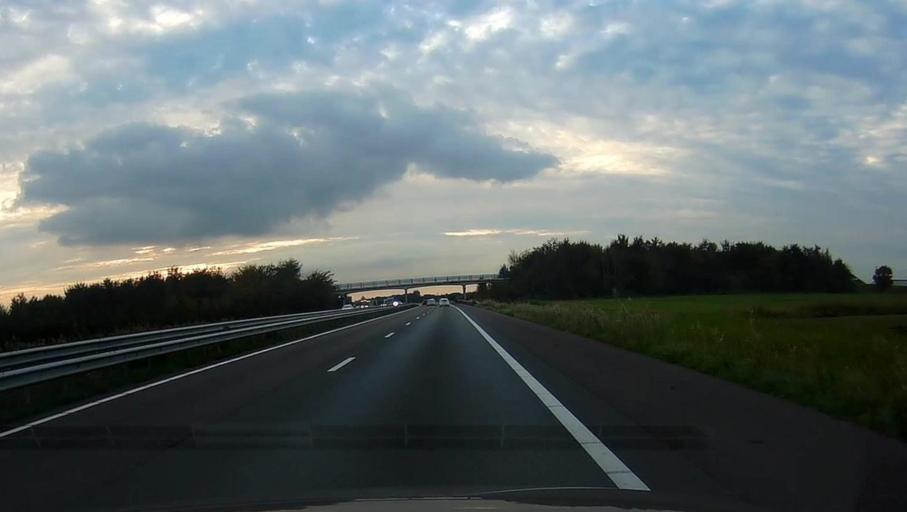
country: NL
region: North Brabant
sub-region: Gemeente Waalwijk
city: Waspik
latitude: 51.6943
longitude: 4.9279
